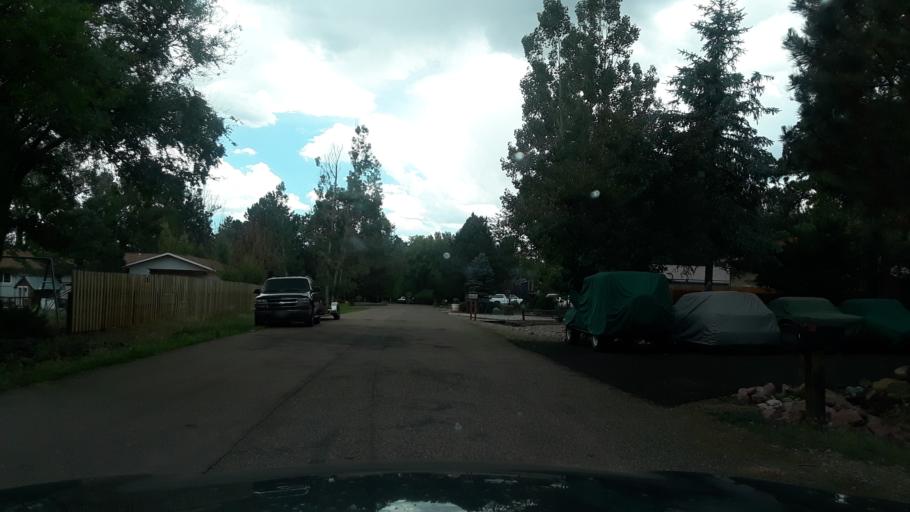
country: US
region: Colorado
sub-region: El Paso County
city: Air Force Academy
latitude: 38.9476
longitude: -104.8263
